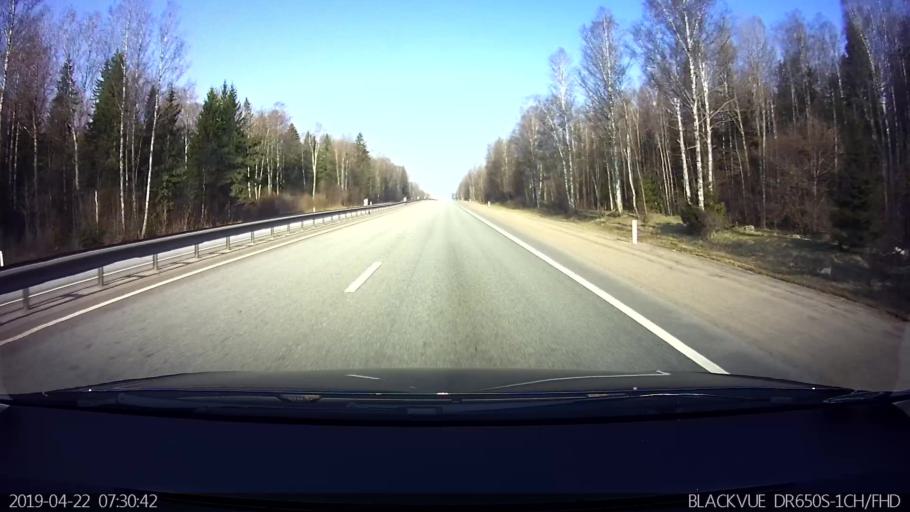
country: RU
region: Smolensk
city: Vyaz'ma
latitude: 55.1942
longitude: 33.9382
